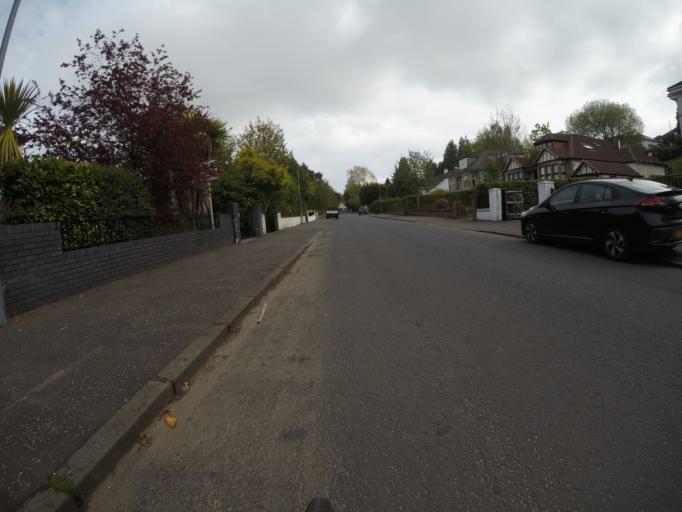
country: GB
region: Scotland
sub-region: East Renfrewshire
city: Giffnock
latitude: 55.7860
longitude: -4.3034
